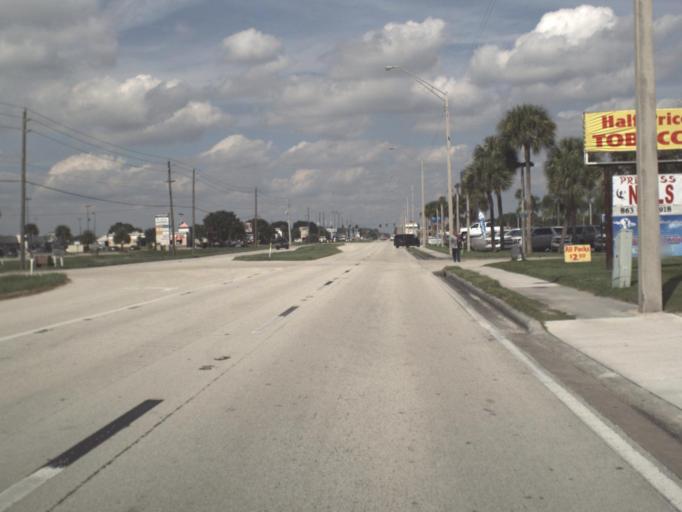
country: US
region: Florida
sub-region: Okeechobee County
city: Okeechobee
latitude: 27.2090
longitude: -80.8297
